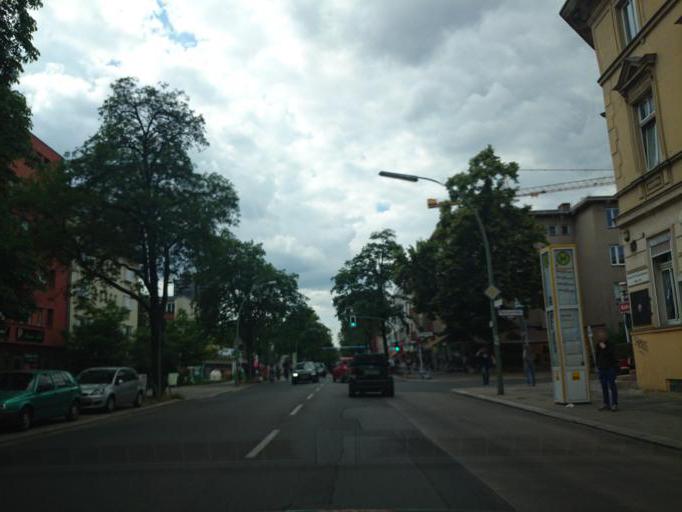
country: DE
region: Berlin
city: Steglitz Bezirk
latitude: 52.4540
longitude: 13.3293
